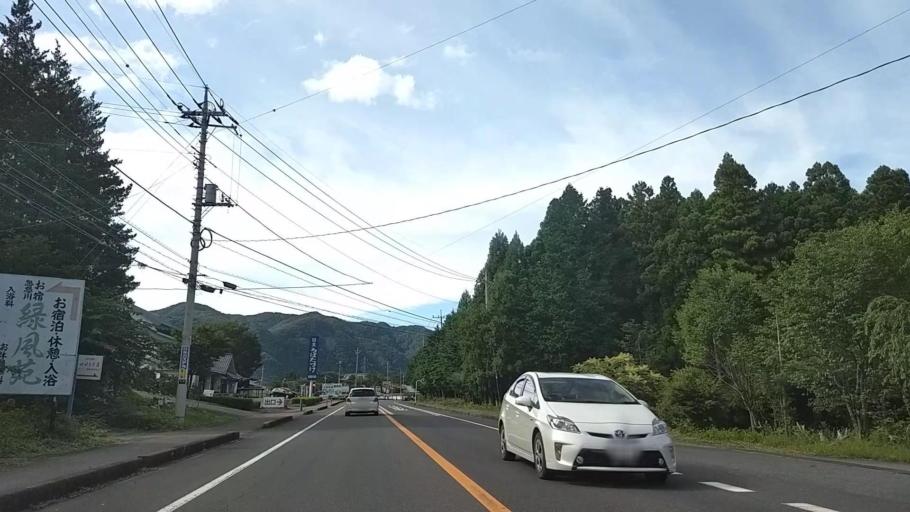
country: JP
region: Tochigi
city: Imaichi
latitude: 36.7770
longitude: 139.7077
